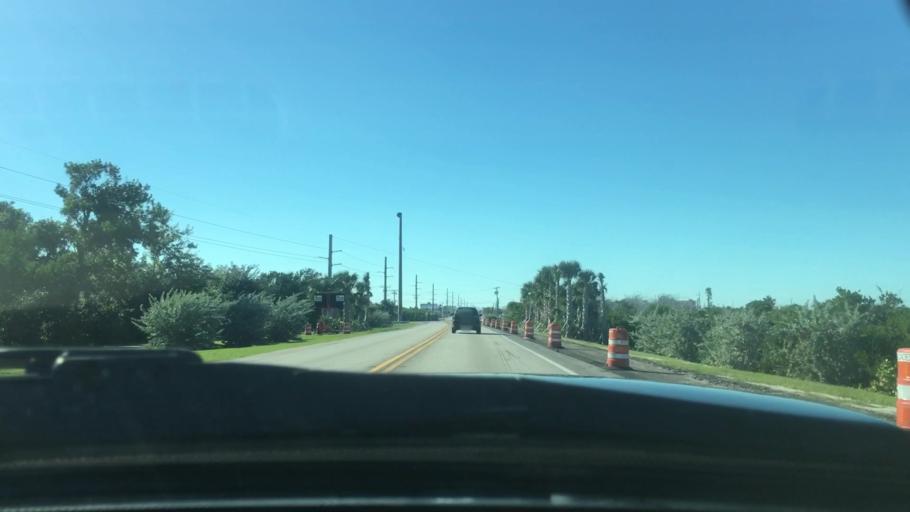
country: US
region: Florida
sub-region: Monroe County
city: Cudjoe Key
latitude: 24.6609
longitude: -81.4372
